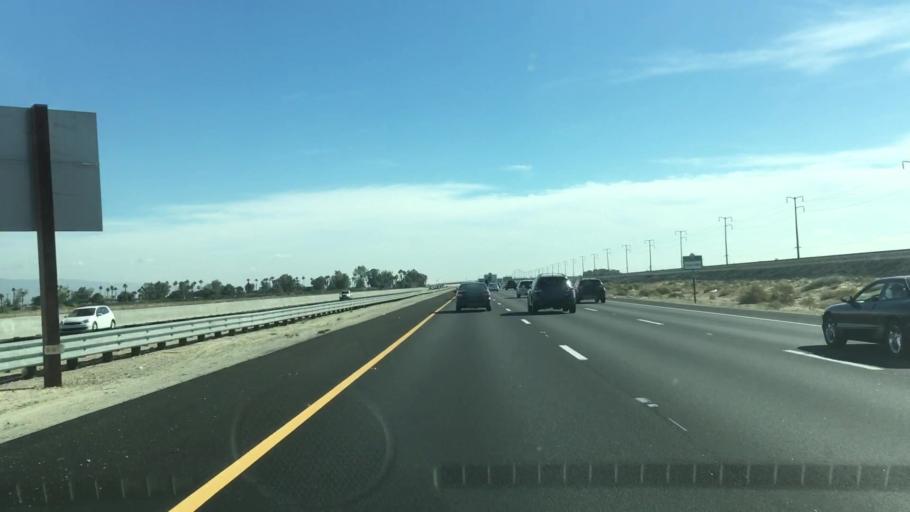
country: US
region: California
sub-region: Riverside County
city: Thousand Palms
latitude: 33.7946
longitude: -116.3692
